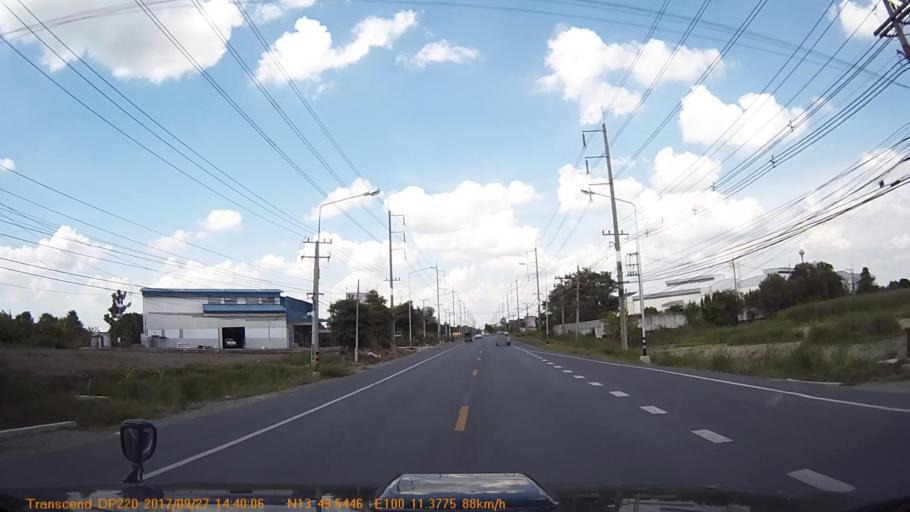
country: TH
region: Nakhon Pathom
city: Nakhon Chai Si
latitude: 13.8257
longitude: 100.1896
